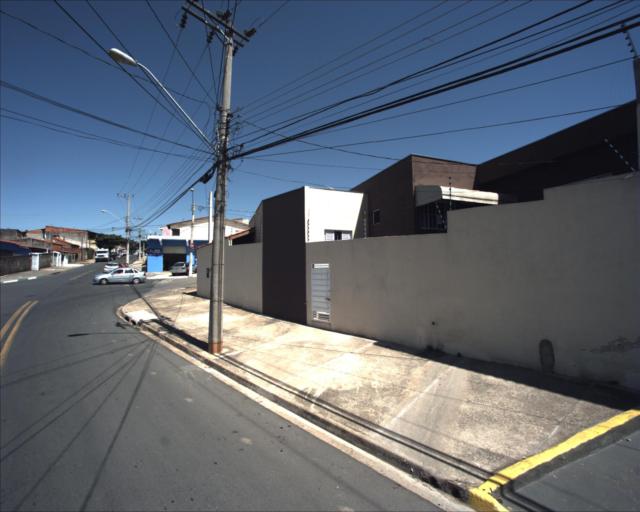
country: BR
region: Sao Paulo
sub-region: Sorocaba
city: Sorocaba
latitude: -23.4731
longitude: -47.4823
